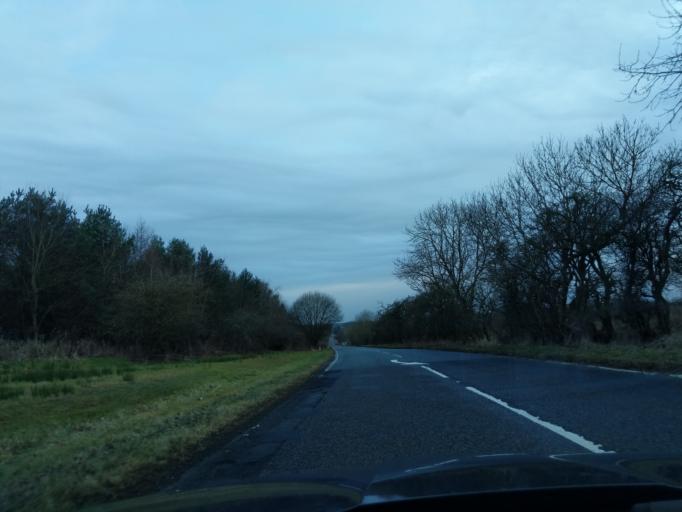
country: GB
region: England
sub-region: Northumberland
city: Rothley
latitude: 55.1378
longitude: -1.9700
